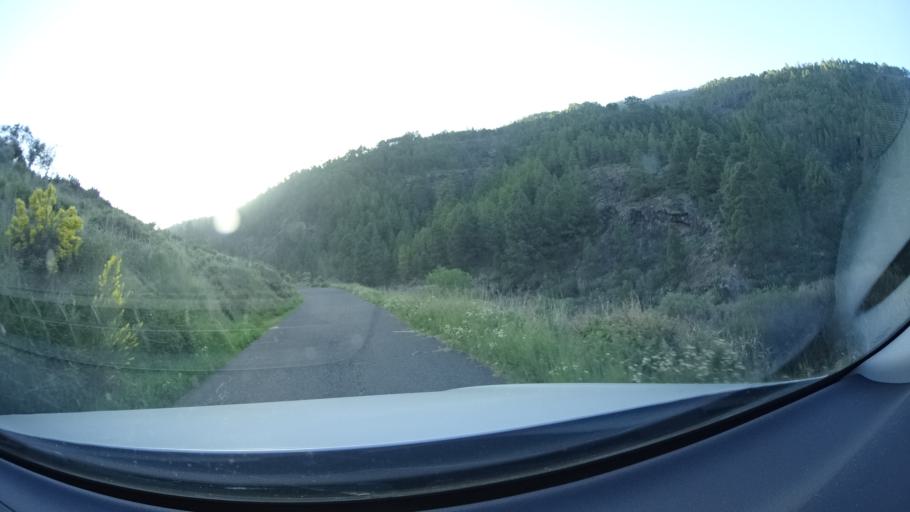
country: ES
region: Canary Islands
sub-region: Provincia de Las Palmas
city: Artenara
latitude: 28.0402
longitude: -15.6760
